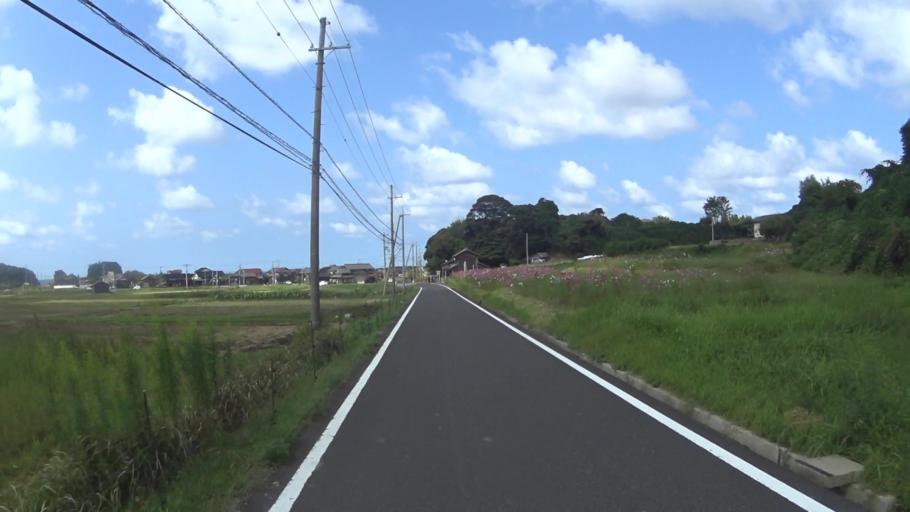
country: JP
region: Kyoto
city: Miyazu
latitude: 35.7539
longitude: 135.1755
